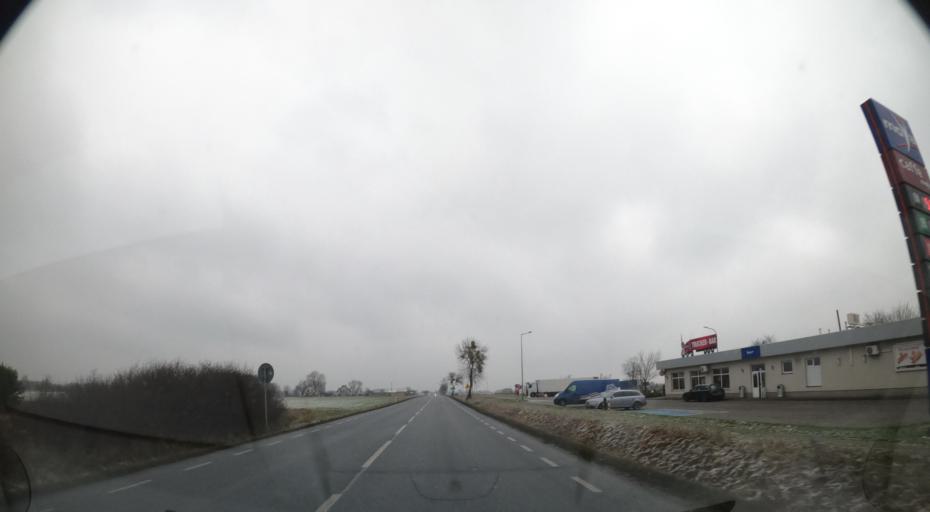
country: PL
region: Masovian Voivodeship
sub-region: Powiat sochaczewski
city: Mlodzieszyn
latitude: 52.2718
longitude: 20.1669
